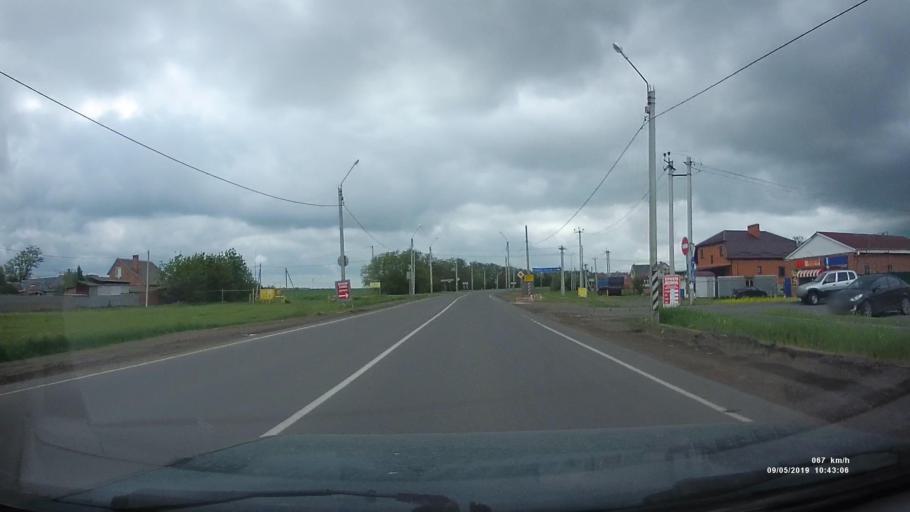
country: RU
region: Rostov
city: Peshkovo
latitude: 47.0115
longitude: 39.4040
